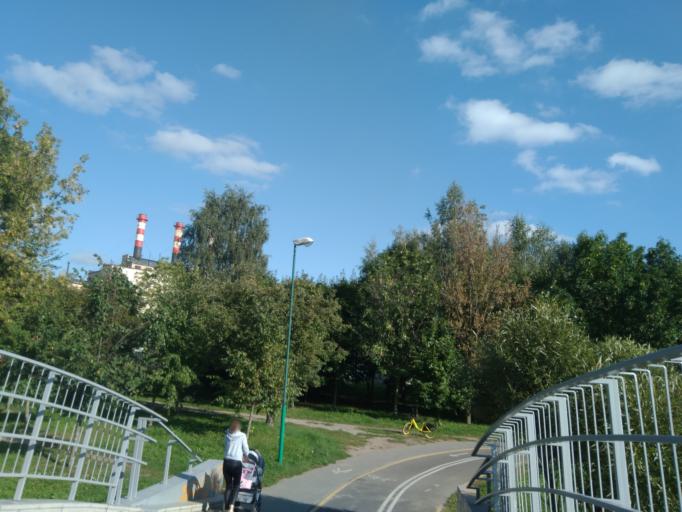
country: BY
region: Minsk
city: Minsk
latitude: 53.8836
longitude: 27.5734
